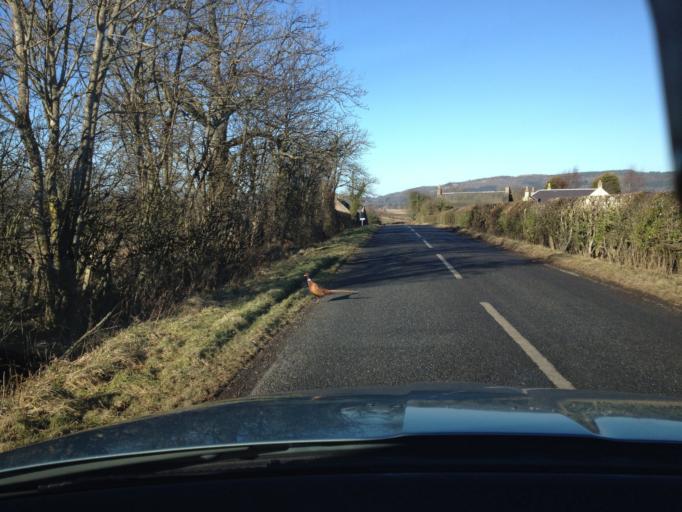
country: GB
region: Scotland
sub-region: Perth and Kinross
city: Bridge of Earn
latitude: 56.3252
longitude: -3.3765
